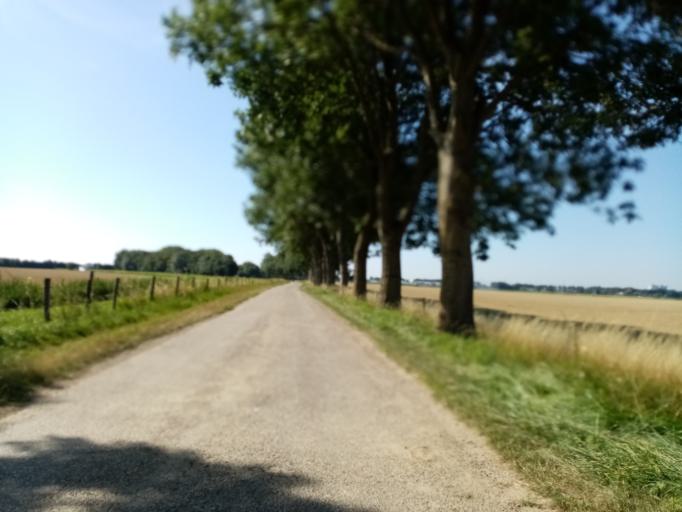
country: NL
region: North Brabant
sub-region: Gemeente Moerdijk
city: Klundert
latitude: 51.6680
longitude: 4.6304
